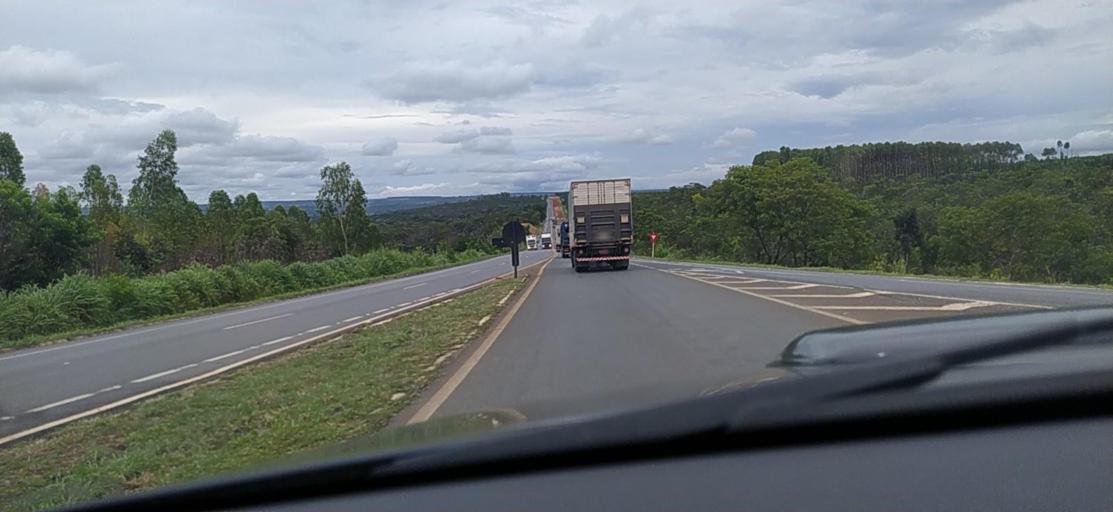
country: BR
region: Minas Gerais
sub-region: Curvelo
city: Curvelo
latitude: -18.7040
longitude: -44.4401
